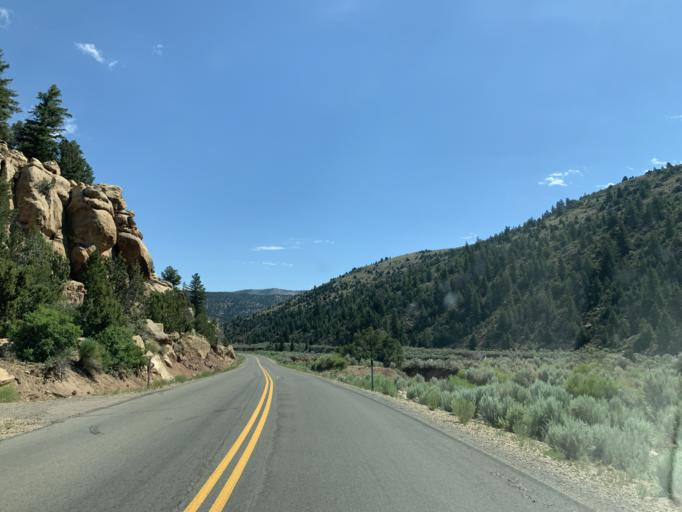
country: US
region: Utah
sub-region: Carbon County
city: East Carbon City
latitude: 39.7624
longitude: -110.5236
